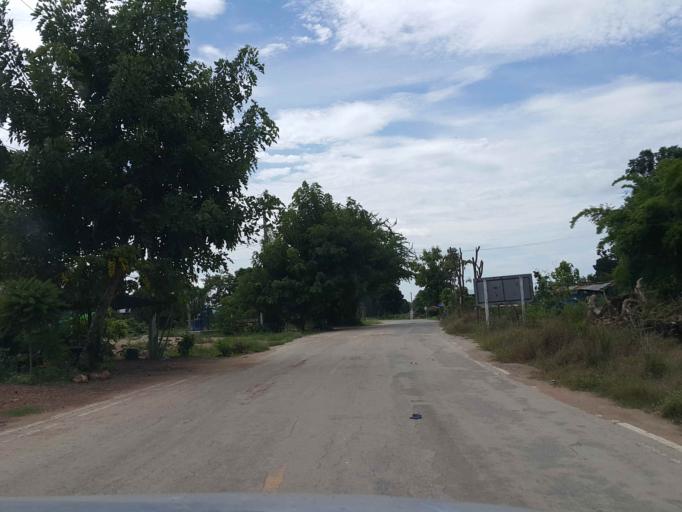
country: TH
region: Sukhothai
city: Ban Dan Lan Hoi
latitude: 17.0742
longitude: 99.4820
